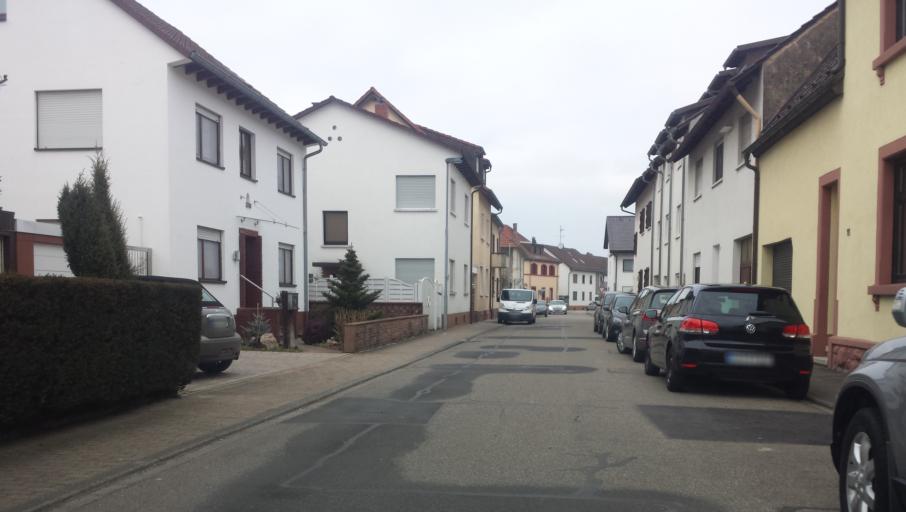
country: DE
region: Baden-Wuerttemberg
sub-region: Karlsruhe Region
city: Heddesheim
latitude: 49.5042
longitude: 8.5980
